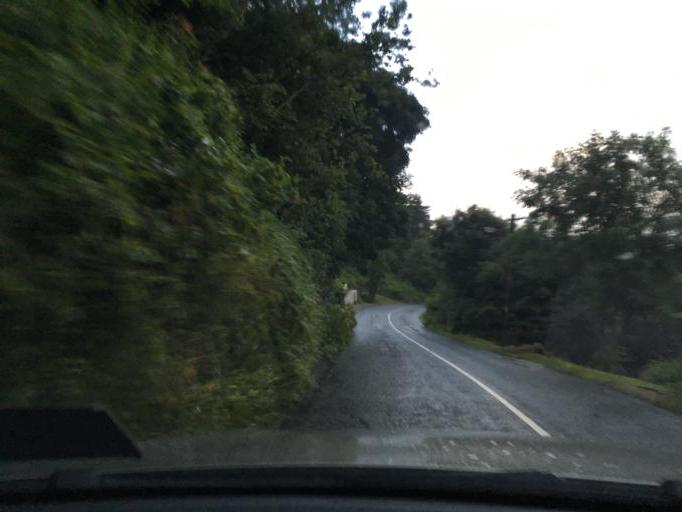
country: IE
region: Ulster
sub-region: County Donegal
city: Killybegs
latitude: 54.6347
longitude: -8.4491
